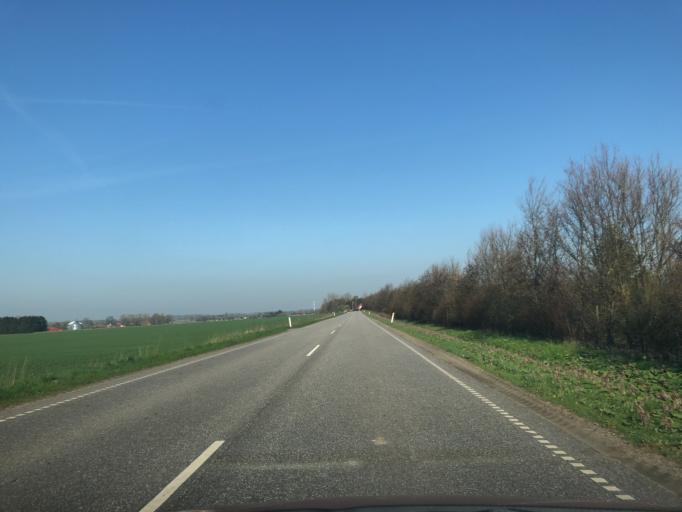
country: DK
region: Zealand
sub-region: Faxe Kommune
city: Haslev
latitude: 55.3552
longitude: 11.9238
